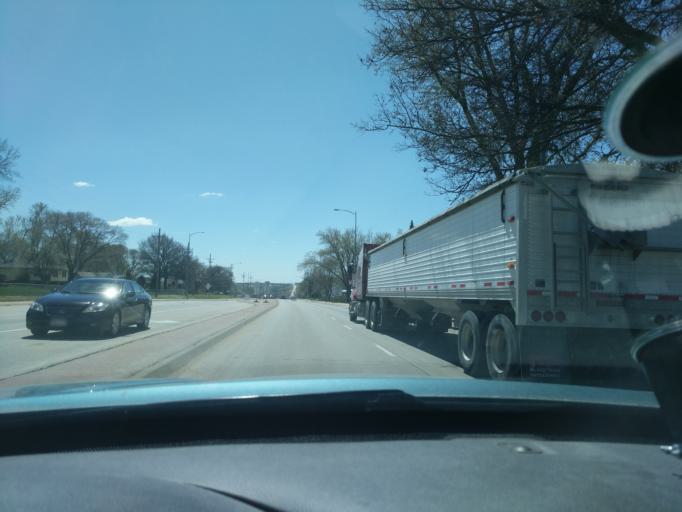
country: US
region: Nebraska
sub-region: Douglas County
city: Elkhorn
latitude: 41.2914
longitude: -96.2344
